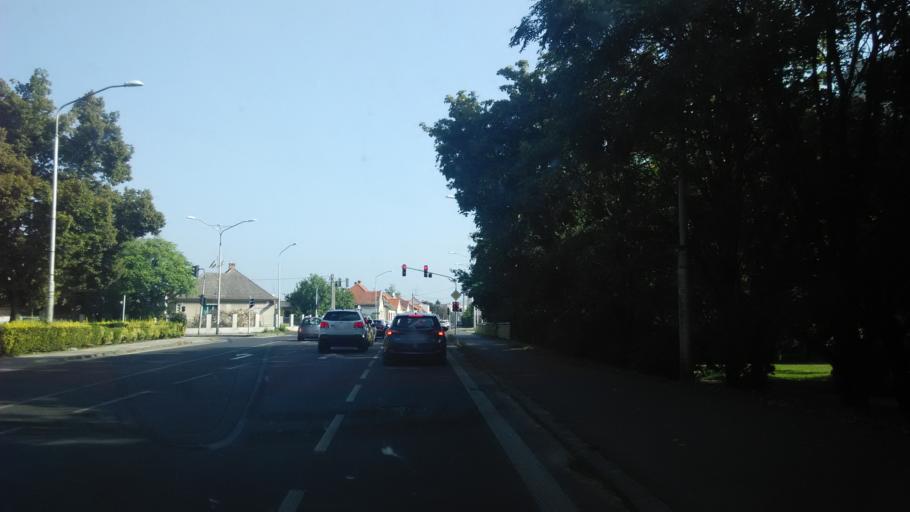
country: SK
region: Trnavsky
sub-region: Okres Trnava
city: Piestany
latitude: 48.5873
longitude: 17.8167
